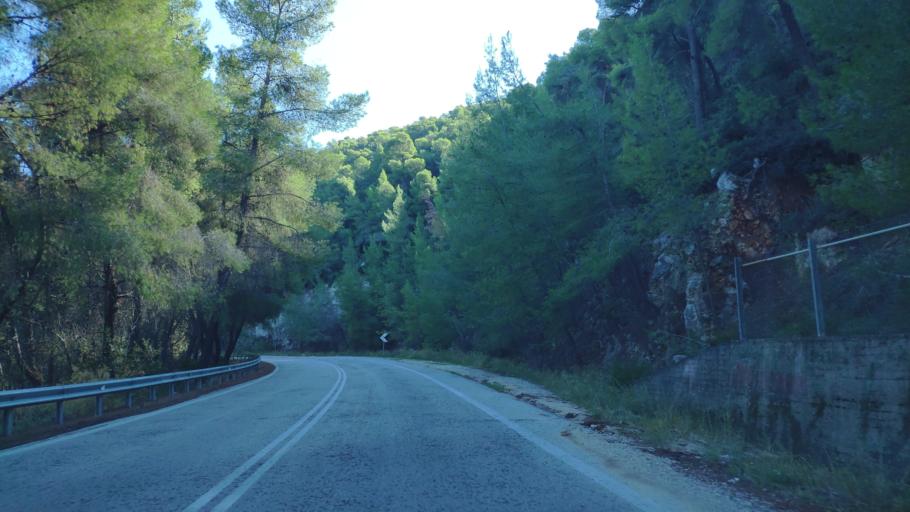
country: GR
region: Peloponnese
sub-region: Nomos Korinthias
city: Sofikon
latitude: 37.8280
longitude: 23.0719
